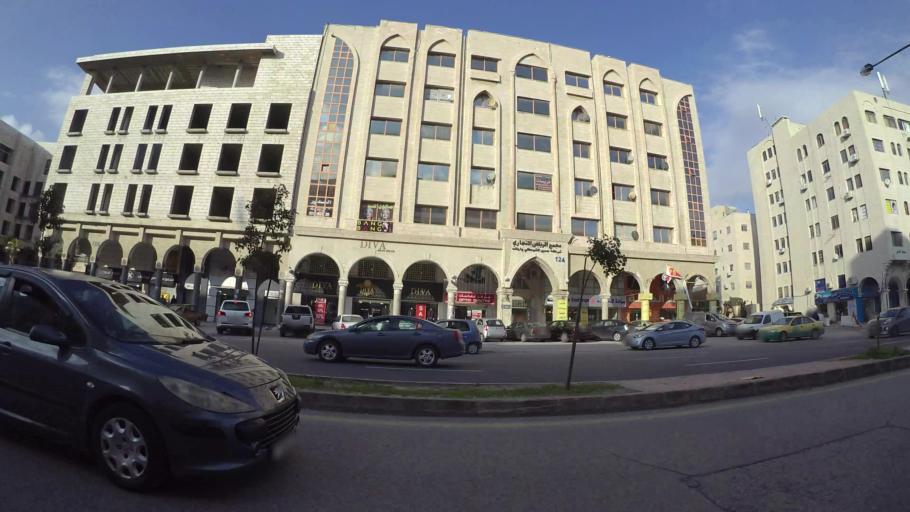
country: JO
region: Amman
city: Al Jubayhah
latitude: 31.9891
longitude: 35.8739
